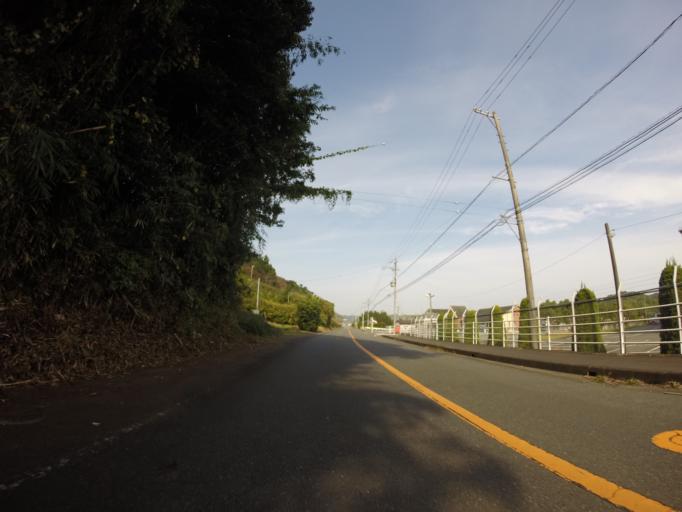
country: JP
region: Shizuoka
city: Shimada
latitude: 34.7601
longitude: 138.1921
